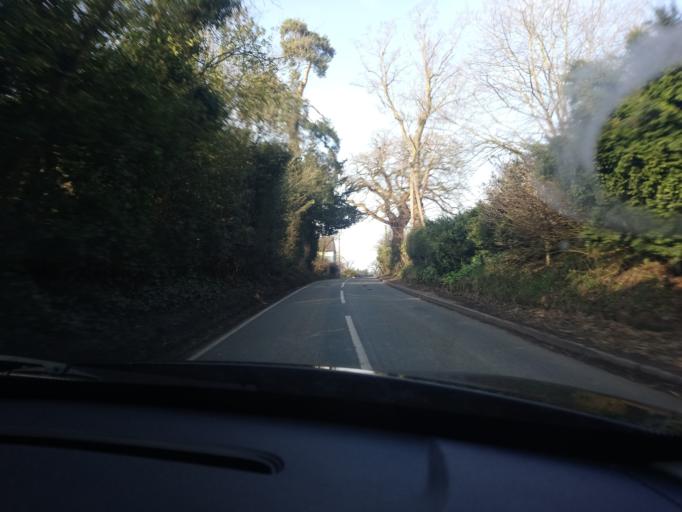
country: GB
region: England
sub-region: Shropshire
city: Shrewsbury
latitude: 52.7363
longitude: -2.7773
